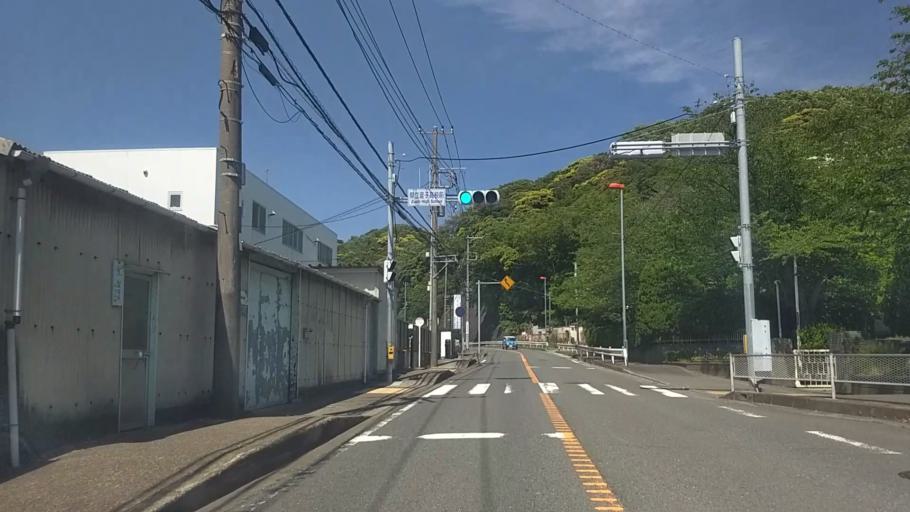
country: JP
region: Kanagawa
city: Zushi
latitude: 35.3106
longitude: 139.5999
